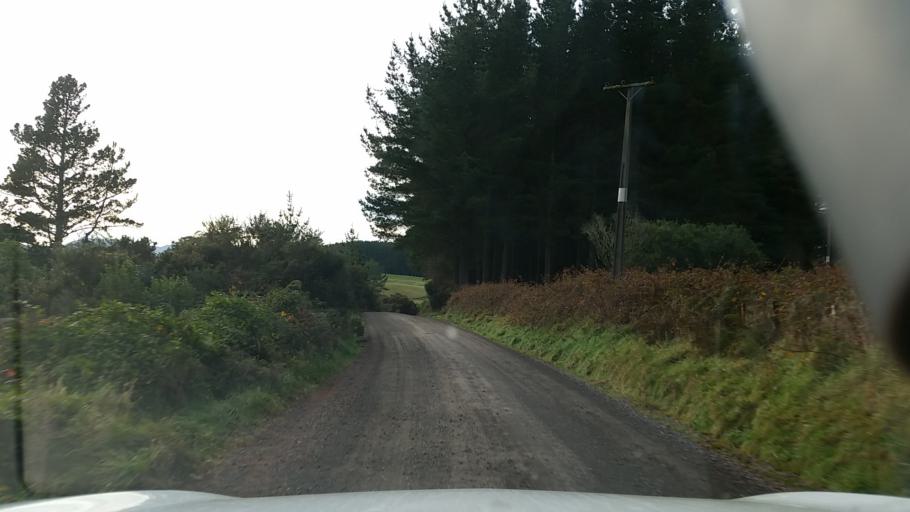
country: NZ
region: Bay of Plenty
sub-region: Rotorua District
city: Rotorua
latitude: -38.2338
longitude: 176.1596
